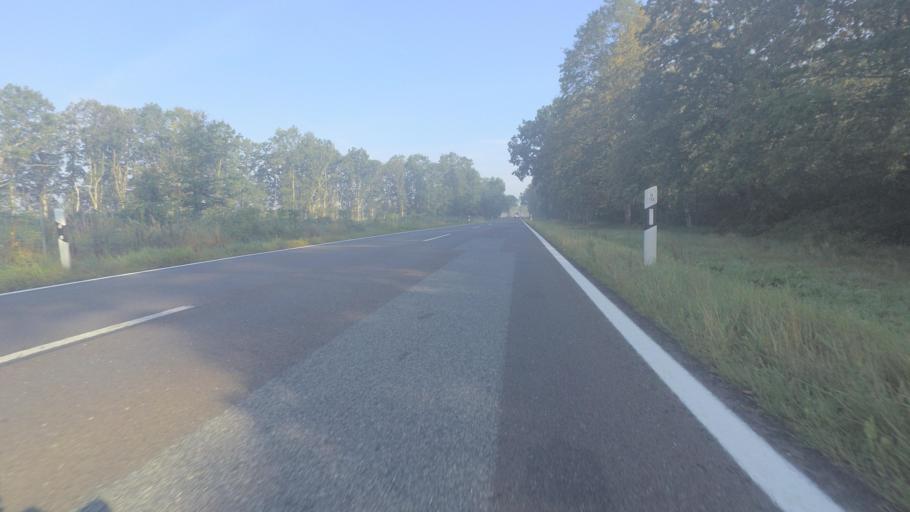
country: DE
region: Mecklenburg-Vorpommern
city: Grimmen
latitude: 54.0290
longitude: 13.1322
